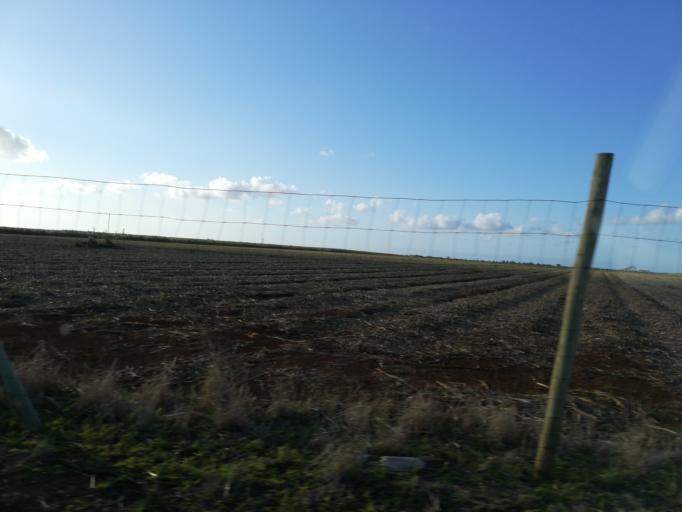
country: MU
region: Pamplemousses
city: Grande Pointe aux Piments
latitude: -20.0808
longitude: 57.5288
